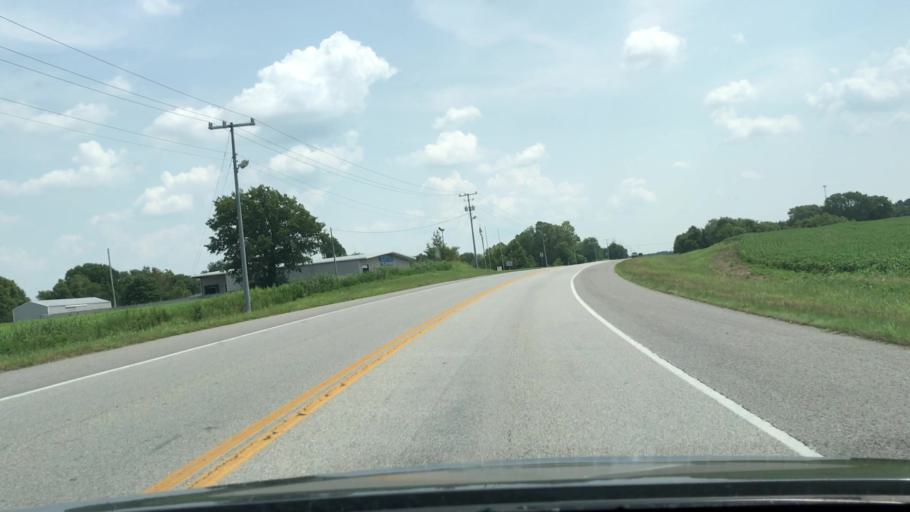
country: US
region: Tennessee
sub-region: Sumner County
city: Portland
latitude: 36.5833
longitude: -86.5704
